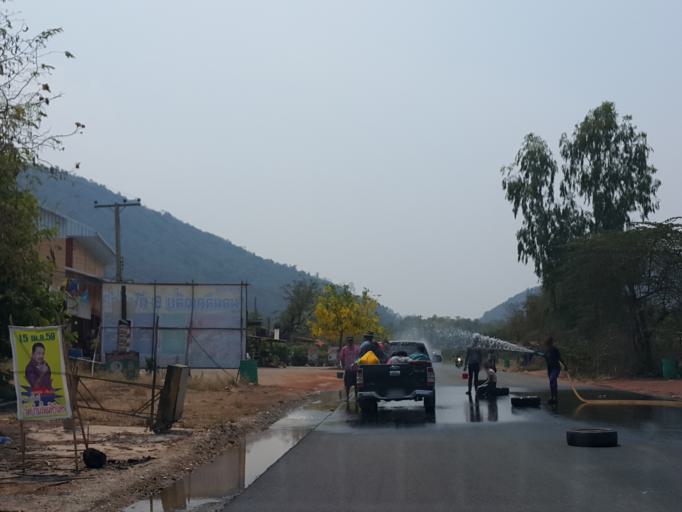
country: TH
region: Nakhon Sawan
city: Mae Wong
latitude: 15.8994
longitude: 99.4665
